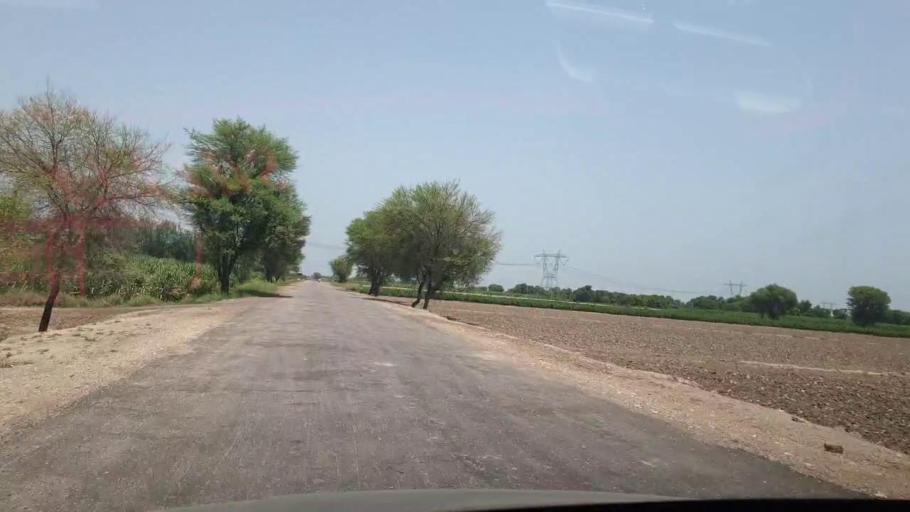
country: PK
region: Sindh
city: Daulatpur
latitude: 26.3894
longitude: 68.0793
